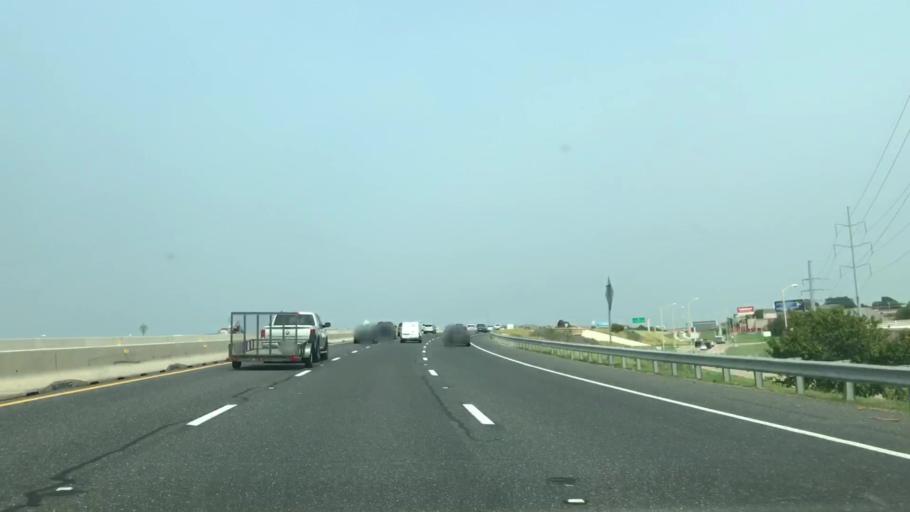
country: US
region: Texas
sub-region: Dallas County
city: Addison
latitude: 33.0122
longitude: -96.8486
